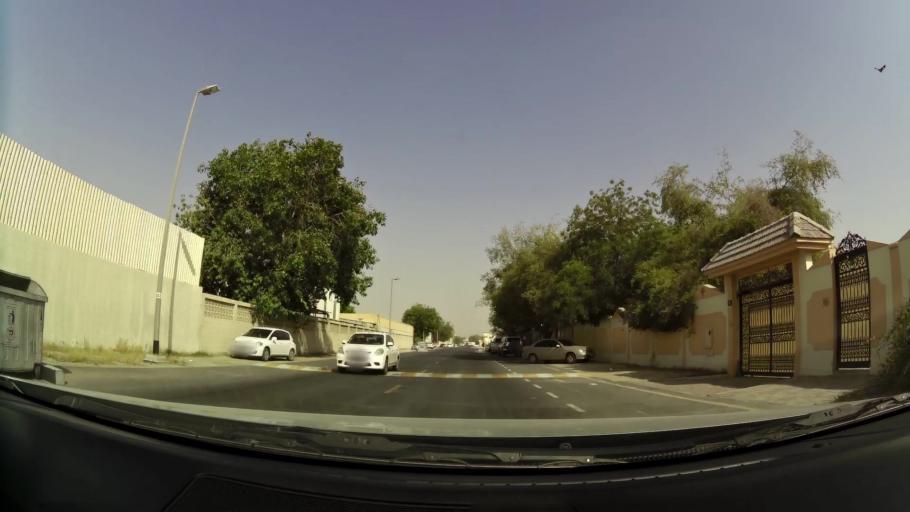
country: AE
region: Dubai
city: Dubai
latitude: 25.1769
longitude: 55.2511
